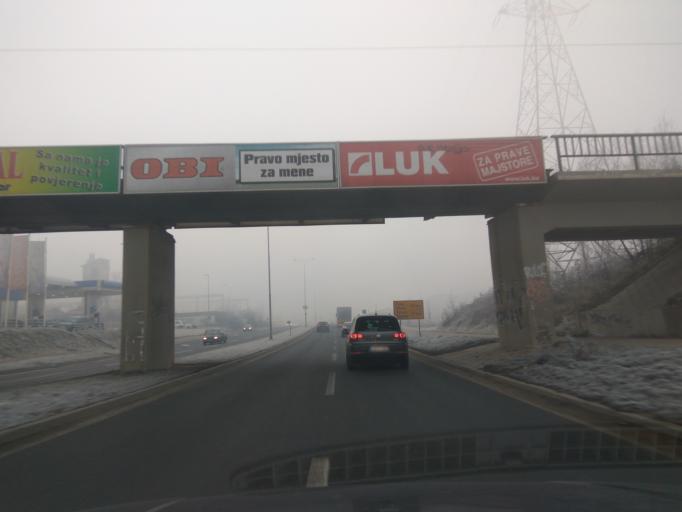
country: BA
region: Federation of Bosnia and Herzegovina
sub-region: Kanton Sarajevo
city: Sarajevo
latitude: 43.8506
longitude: 18.3266
